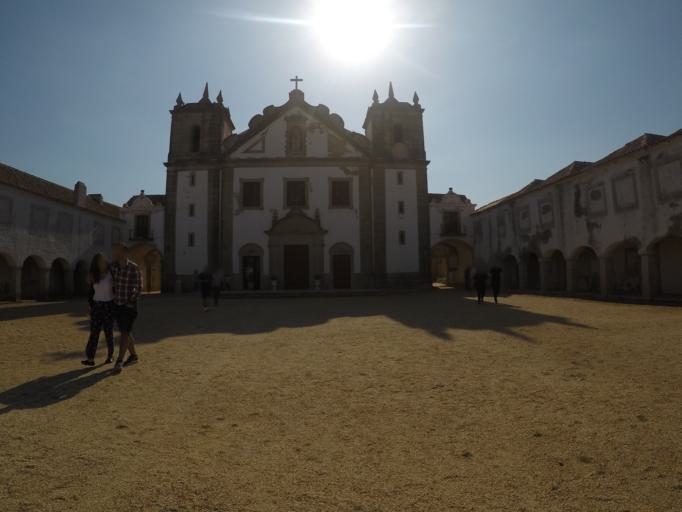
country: PT
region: Setubal
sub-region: Sesimbra
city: Sesimbra
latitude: 38.4202
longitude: -9.2151
